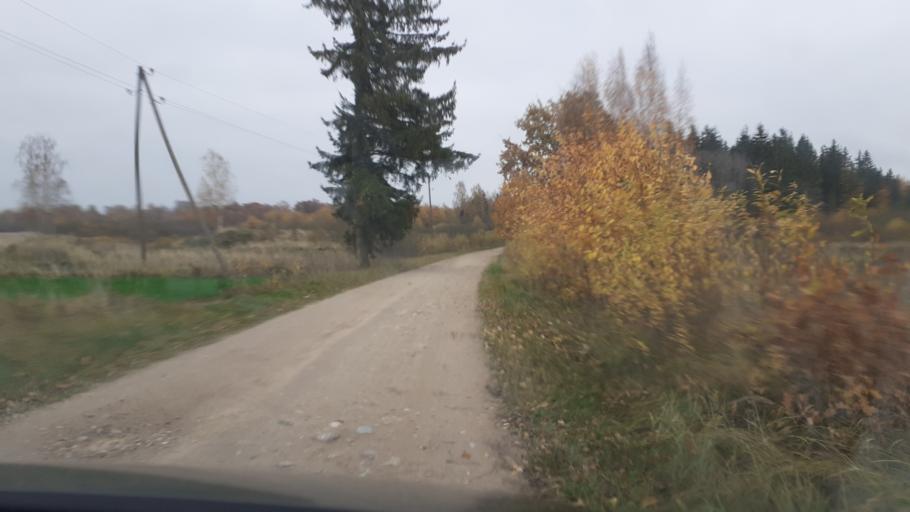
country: LV
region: Saldus Rajons
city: Saldus
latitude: 56.8624
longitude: 22.3293
